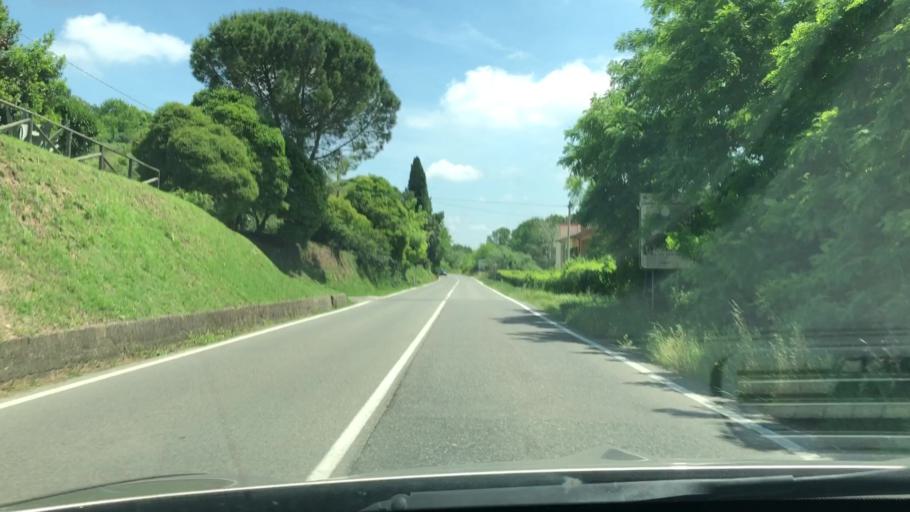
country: IT
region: Tuscany
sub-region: Province of Pisa
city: Forcoli
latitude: 43.6074
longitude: 10.6951
